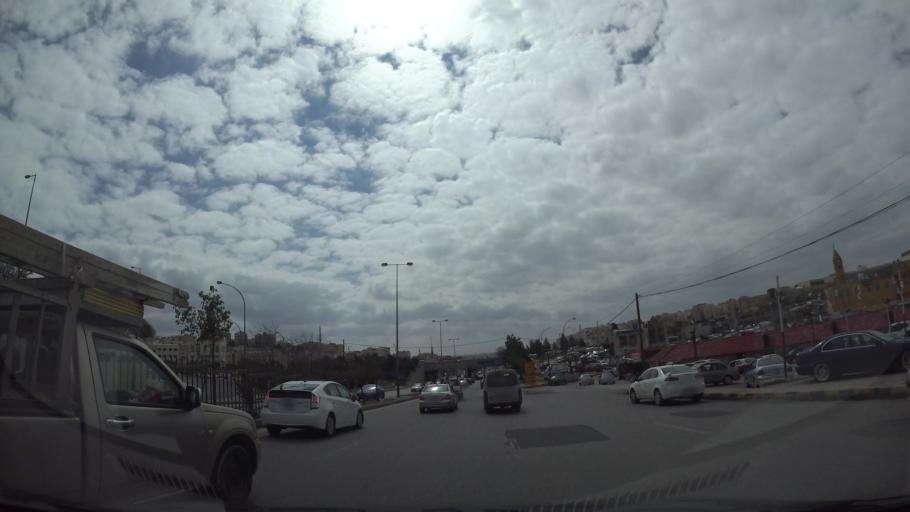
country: JO
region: Amman
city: Amman
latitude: 31.9948
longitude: 35.9184
